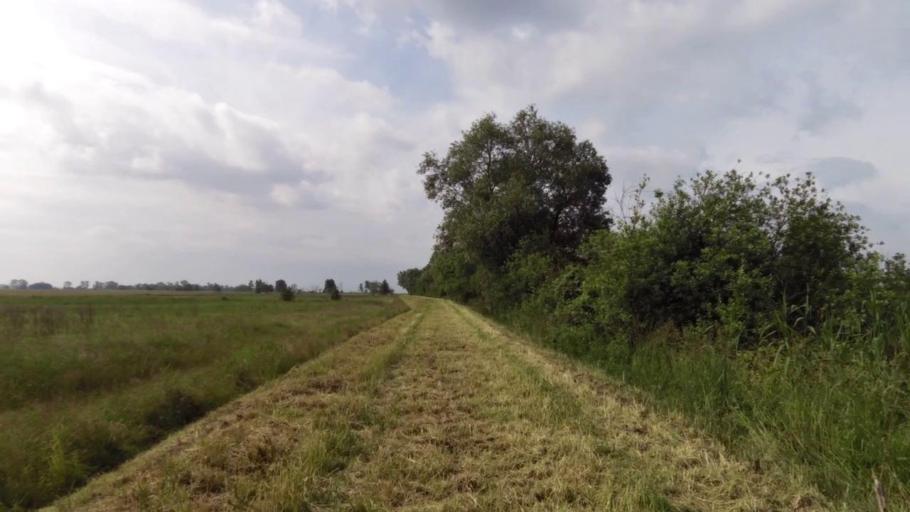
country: PL
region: West Pomeranian Voivodeship
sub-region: Powiat policki
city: Police
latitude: 53.5413
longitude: 14.6783
